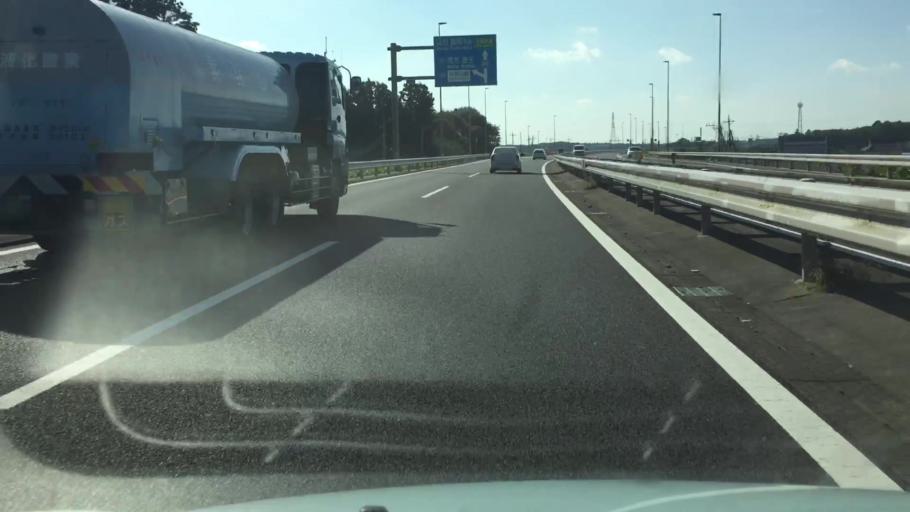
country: JP
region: Tochigi
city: Mooka
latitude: 36.4941
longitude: 139.9912
